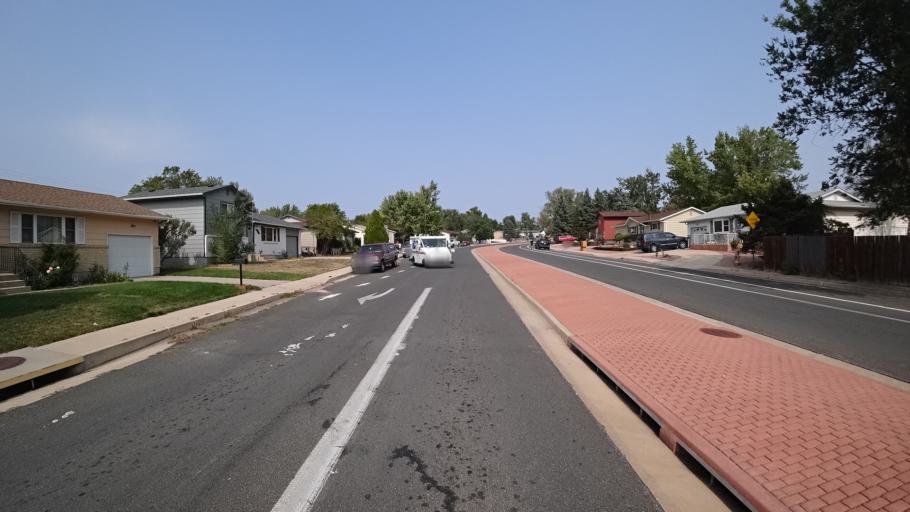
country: US
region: Colorado
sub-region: El Paso County
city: Stratmoor
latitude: 38.7964
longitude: -104.7660
